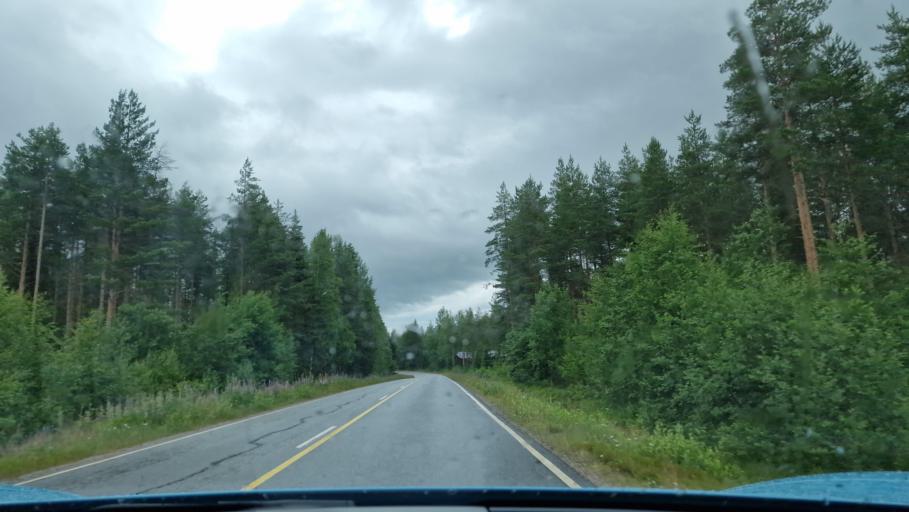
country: FI
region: Southern Ostrobothnia
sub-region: Jaerviseutu
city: Soini
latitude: 62.7746
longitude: 24.3872
